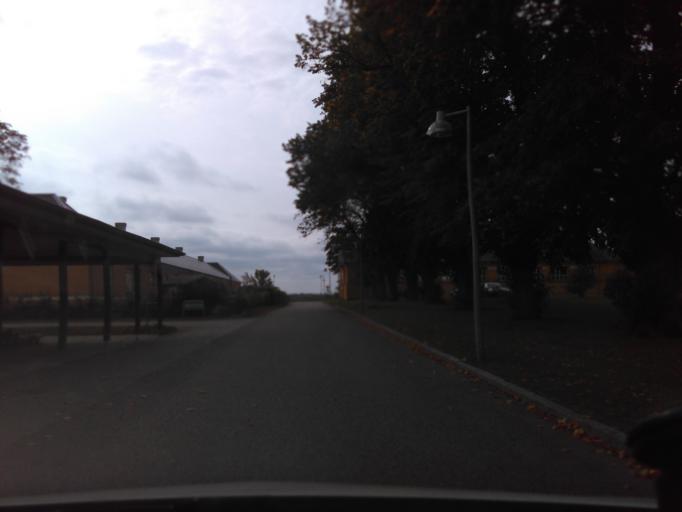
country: DK
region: Capital Region
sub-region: Ballerup Kommune
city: Malov
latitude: 55.7758
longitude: 12.3227
